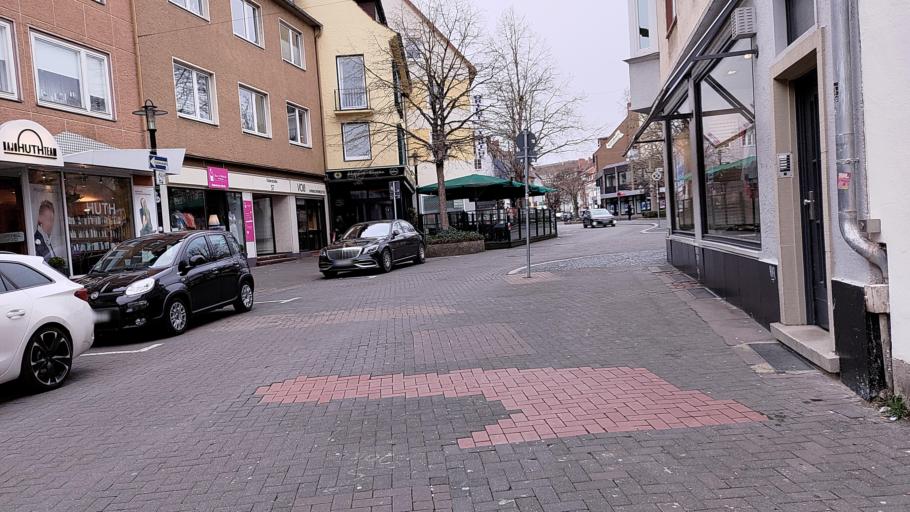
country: DE
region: Lower Saxony
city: Hildesheim
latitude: 52.1529
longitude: 9.9542
